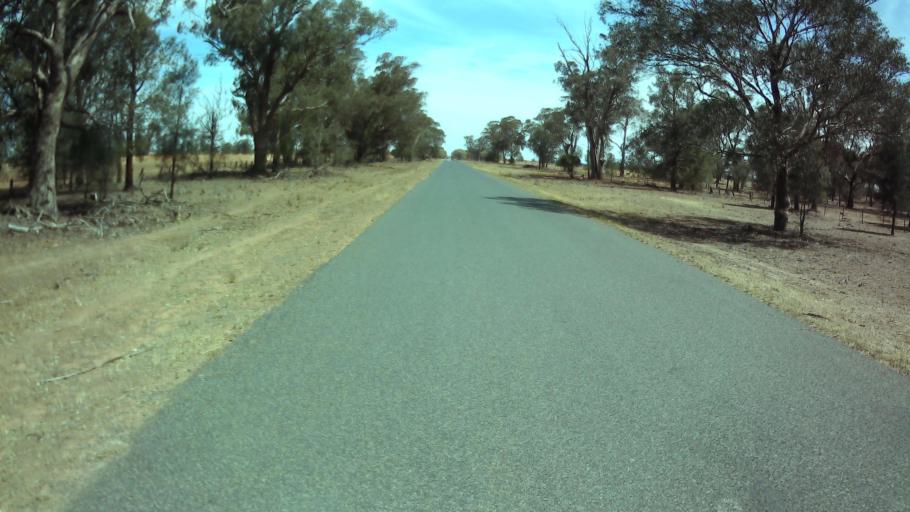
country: AU
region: New South Wales
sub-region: Weddin
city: Grenfell
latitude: -33.8649
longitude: 147.7458
